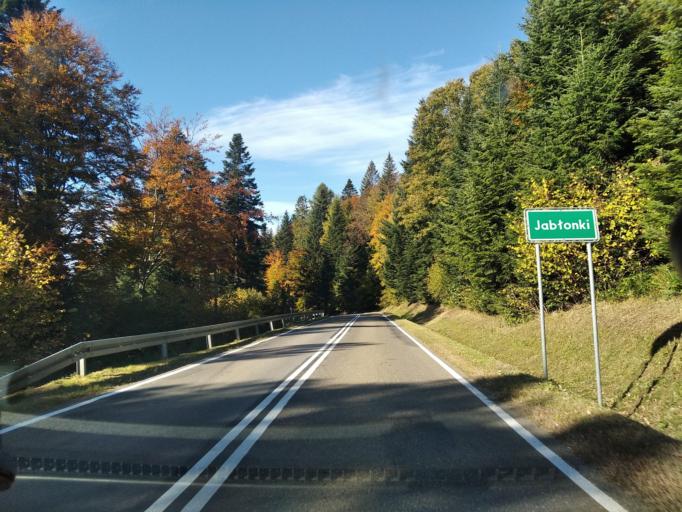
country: PL
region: Subcarpathian Voivodeship
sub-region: Powiat leski
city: Cisna
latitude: 49.2415
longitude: 22.2972
